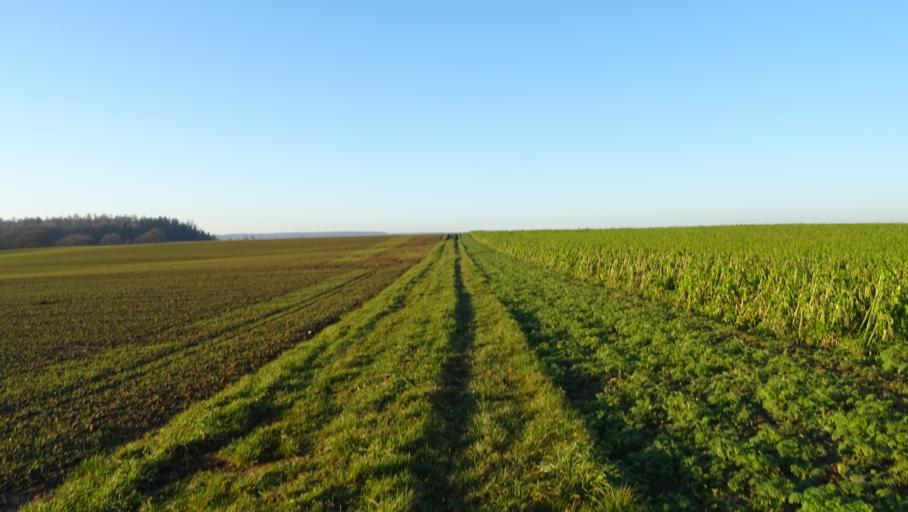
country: DE
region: Baden-Wuerttemberg
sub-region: Karlsruhe Region
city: Aglasterhausen
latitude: 49.3426
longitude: 8.9998
